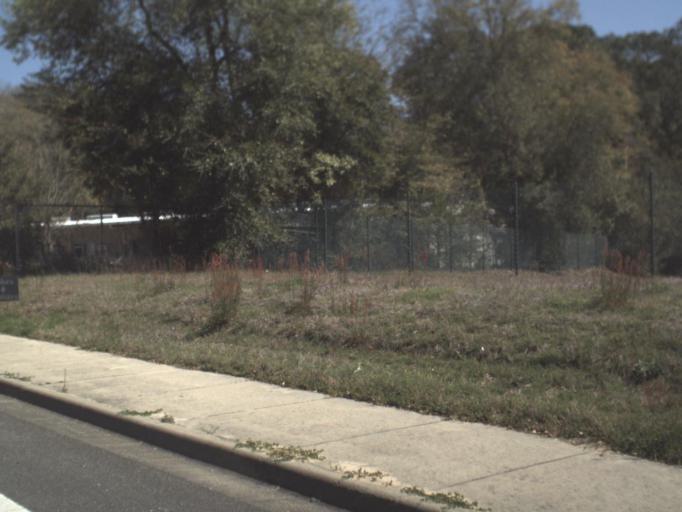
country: US
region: Florida
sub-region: Leon County
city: Tallahassee
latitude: 30.3857
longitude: -84.2876
